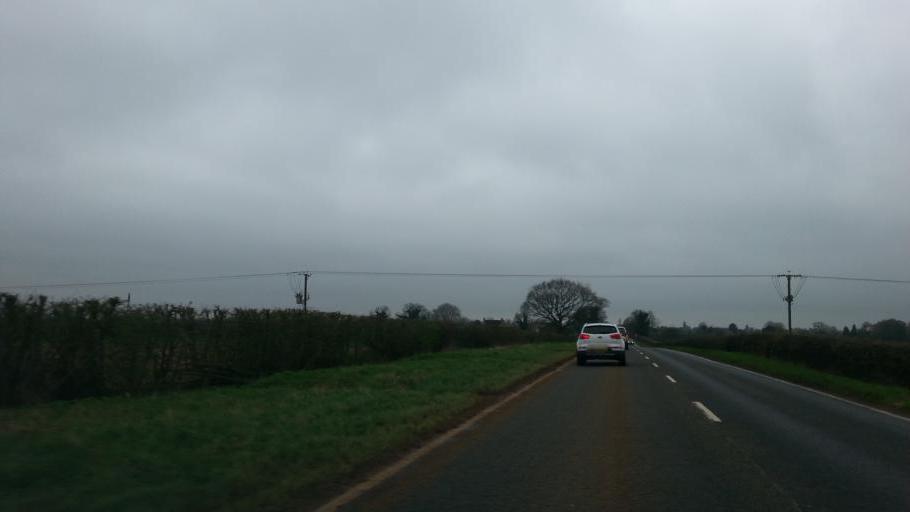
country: GB
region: England
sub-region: Oxfordshire
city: Adderbury
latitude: 52.0655
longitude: -1.2536
